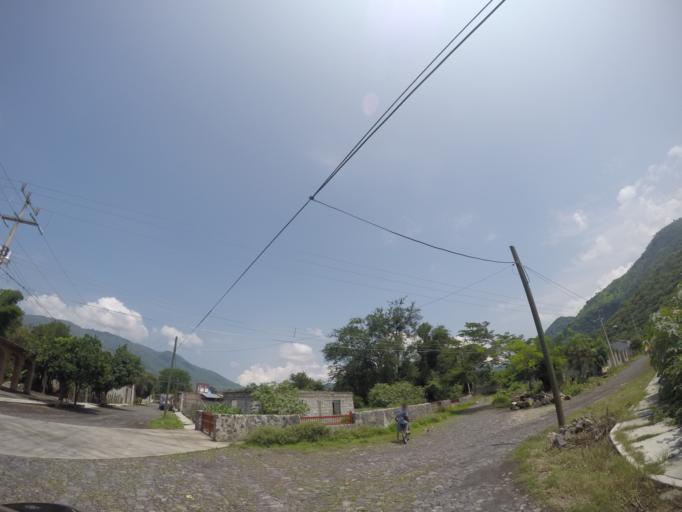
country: MX
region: Nayarit
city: Jala
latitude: 21.1082
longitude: -104.4347
